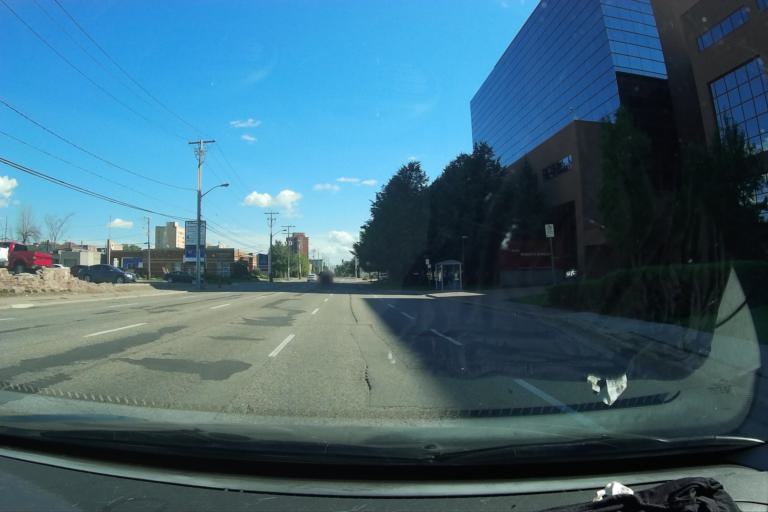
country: CA
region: Ontario
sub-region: Algoma
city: Sault Ste. Marie
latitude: 46.5104
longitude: -84.3340
